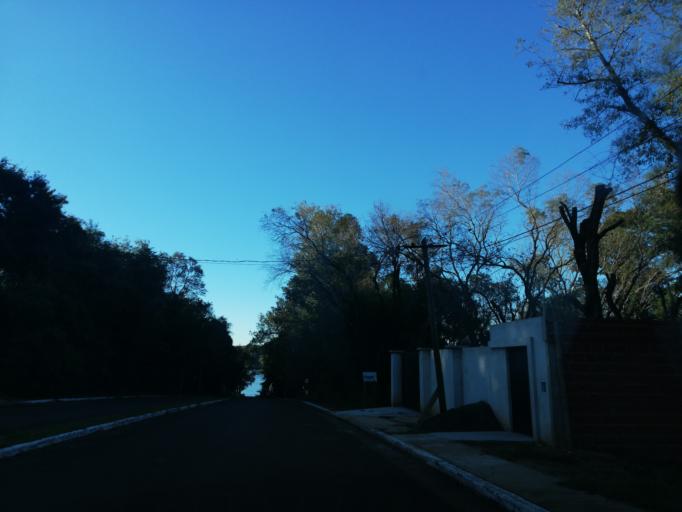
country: AR
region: Misiones
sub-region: Departamento de Candelaria
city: Candelaria
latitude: -27.4500
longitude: -55.7471
